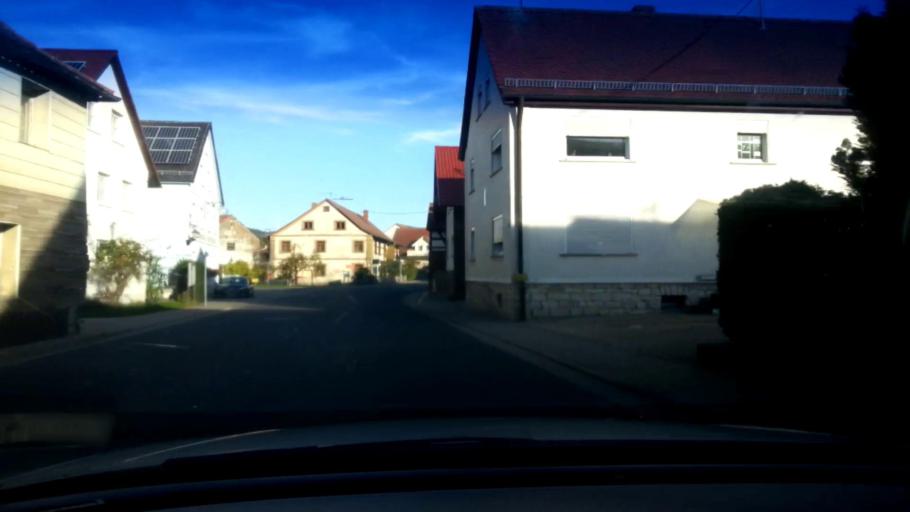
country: DE
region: Bavaria
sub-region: Upper Franconia
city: Litzendorf
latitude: 49.9162
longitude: 11.0441
